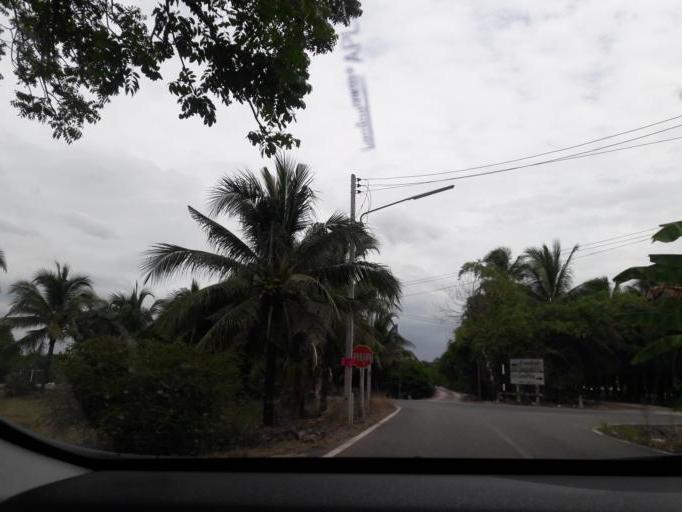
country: TH
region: Ratchaburi
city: Damnoen Saduak
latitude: 13.5632
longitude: 99.9792
